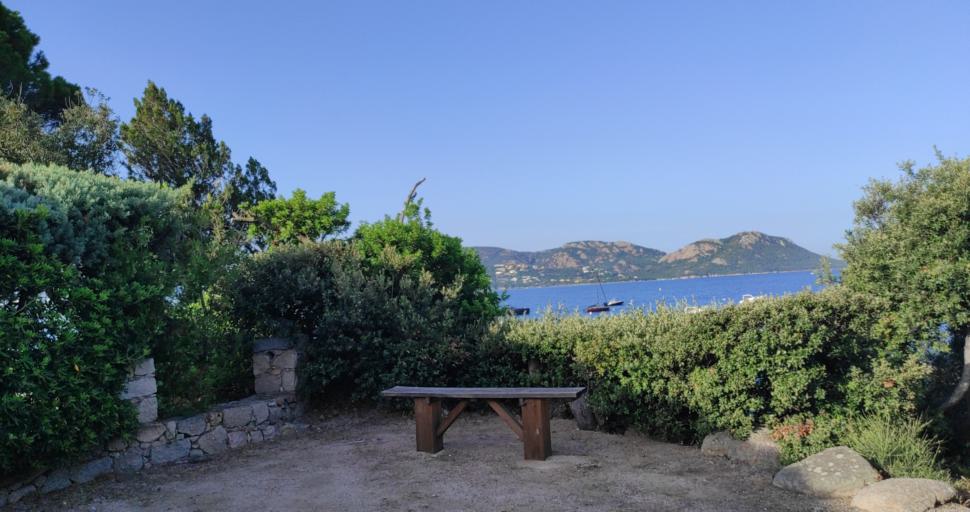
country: FR
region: Corsica
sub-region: Departement de la Corse-du-Sud
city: Porto-Vecchio
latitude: 41.6187
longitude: 9.3527
